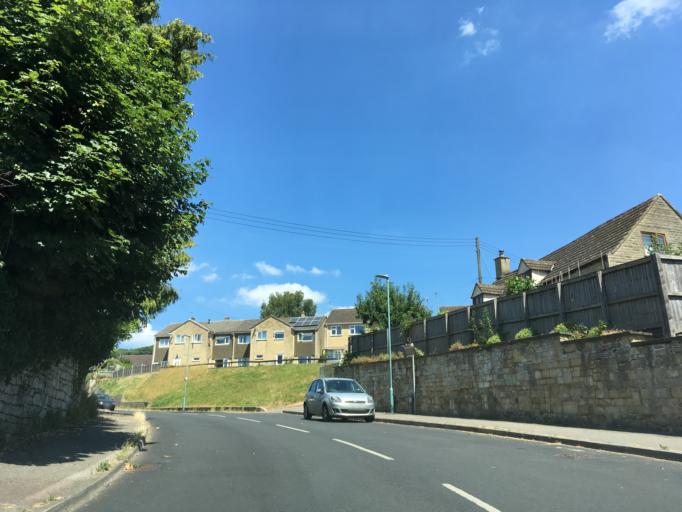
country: GB
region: England
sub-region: Gloucestershire
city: Stroud
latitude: 51.7388
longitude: -2.2051
